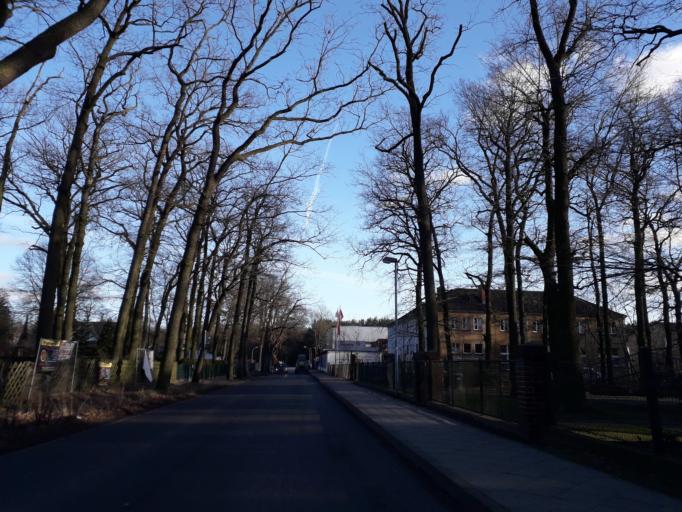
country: DE
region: Brandenburg
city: Brieselang
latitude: 52.5792
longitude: 13.0024
